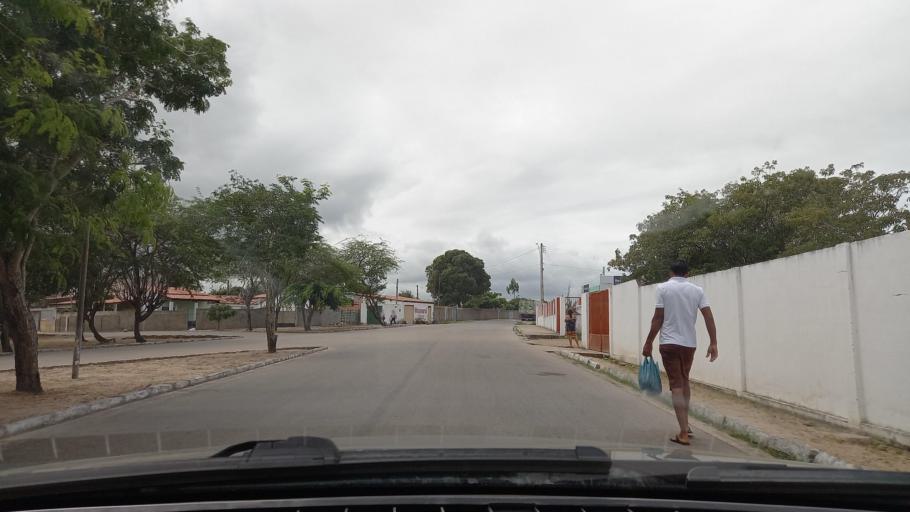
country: BR
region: Sergipe
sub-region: Caninde De Sao Francisco
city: Caninde de Sao Francisco
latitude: -9.6033
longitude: -37.7589
